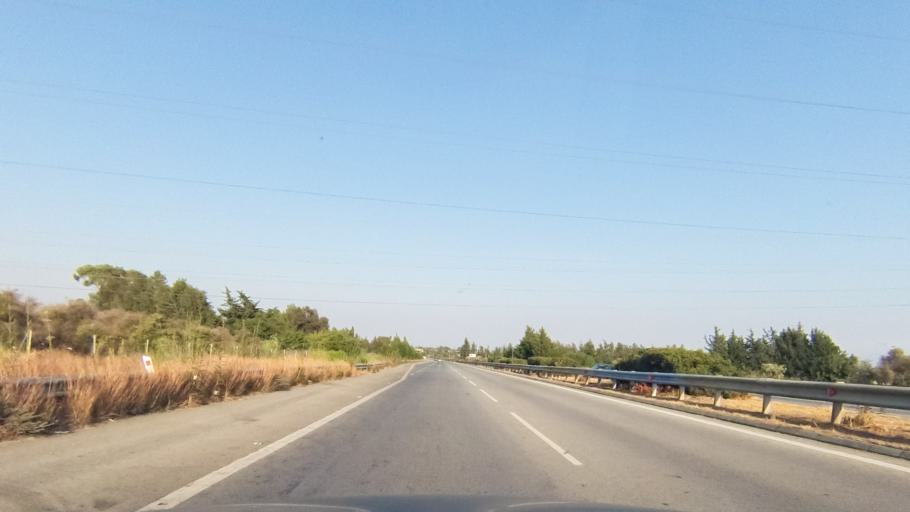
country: CY
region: Limassol
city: Ypsonas
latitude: 34.6902
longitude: 32.9809
